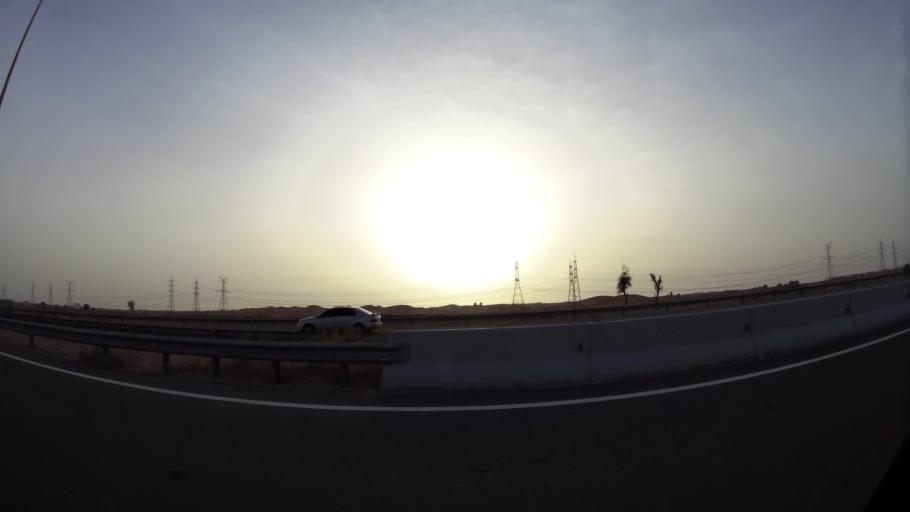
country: OM
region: Al Buraimi
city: Al Buraymi
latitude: 24.3114
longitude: 55.7476
